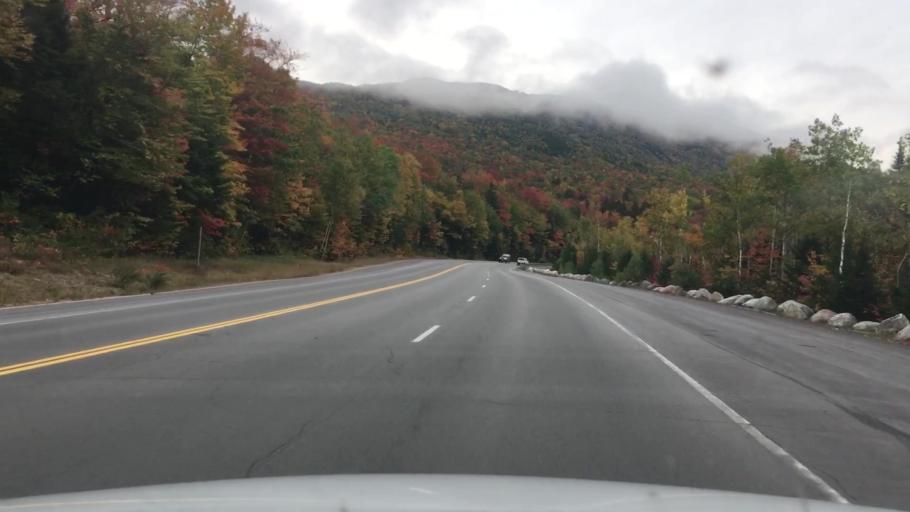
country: US
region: New Hampshire
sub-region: Coos County
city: Gorham
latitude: 44.2771
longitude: -71.2321
